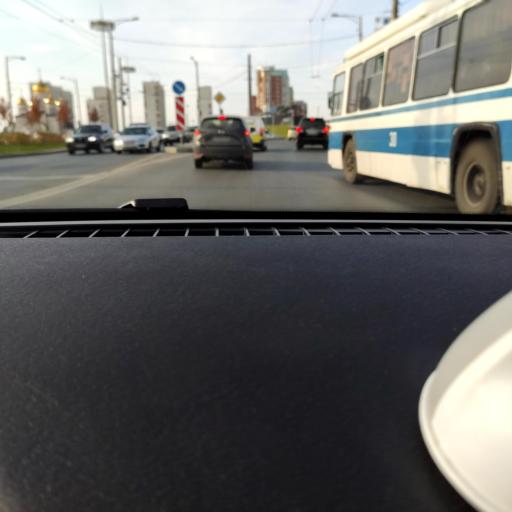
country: RU
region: Samara
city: Samara
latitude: 53.2504
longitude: 50.2246
